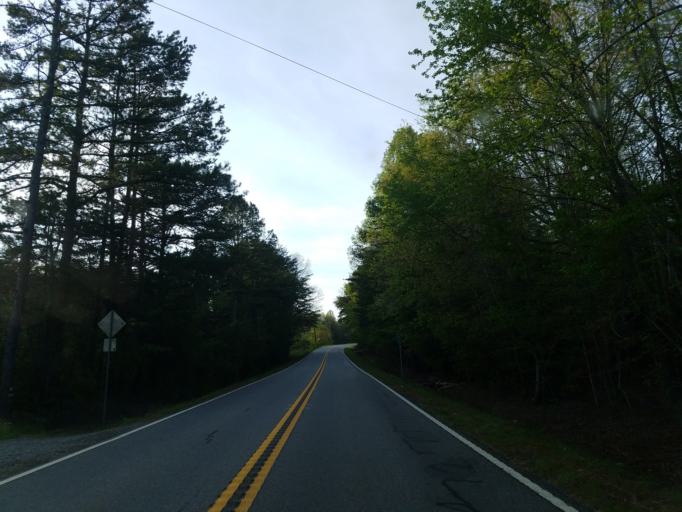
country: US
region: Georgia
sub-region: Fannin County
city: Blue Ridge
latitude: 34.8484
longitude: -84.2178
